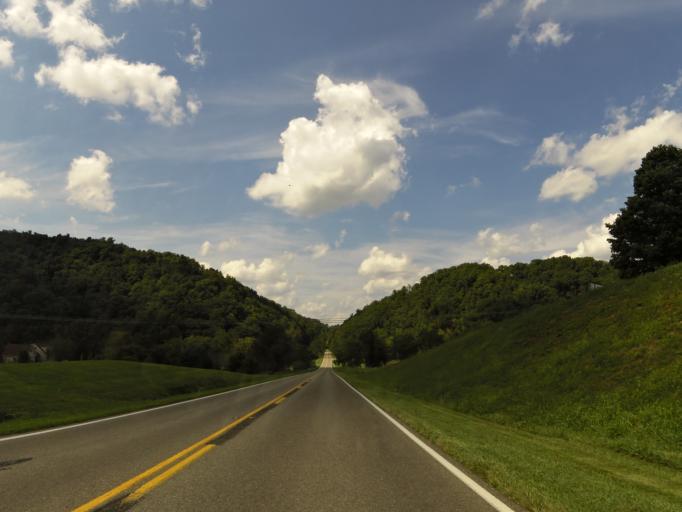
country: US
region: Virginia
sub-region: Washington County
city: Abingdon
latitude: 36.6675
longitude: -81.9670
